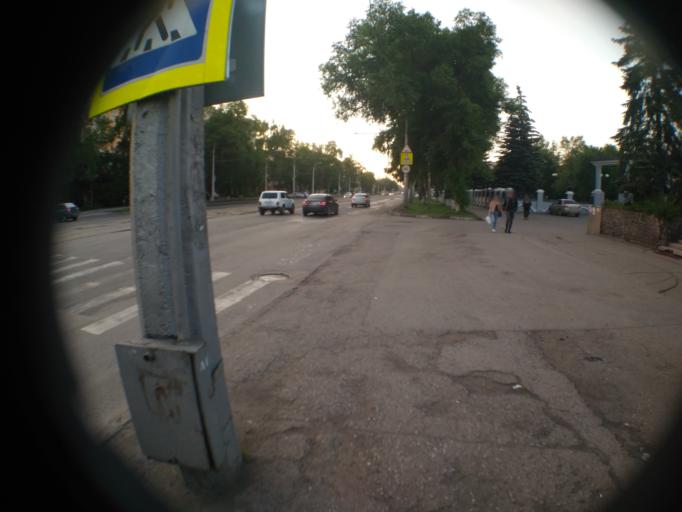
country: RU
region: Kemerovo
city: Novokuznetsk
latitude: 53.7545
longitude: 87.1185
